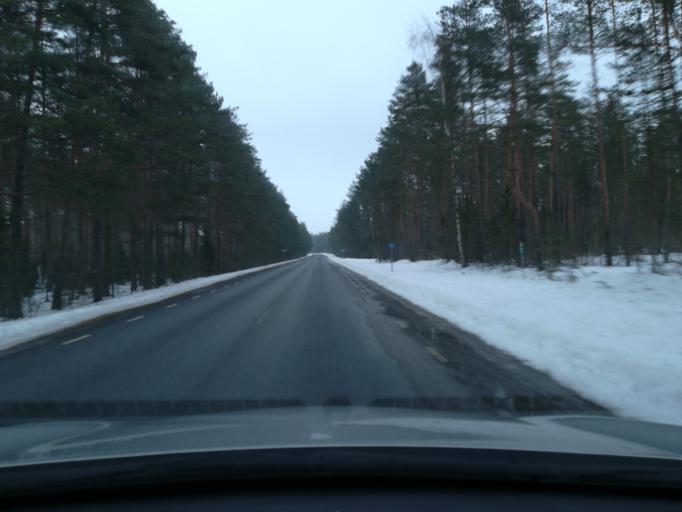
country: EE
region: Harju
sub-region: Kuusalu vald
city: Kuusalu
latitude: 59.4605
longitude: 25.4928
